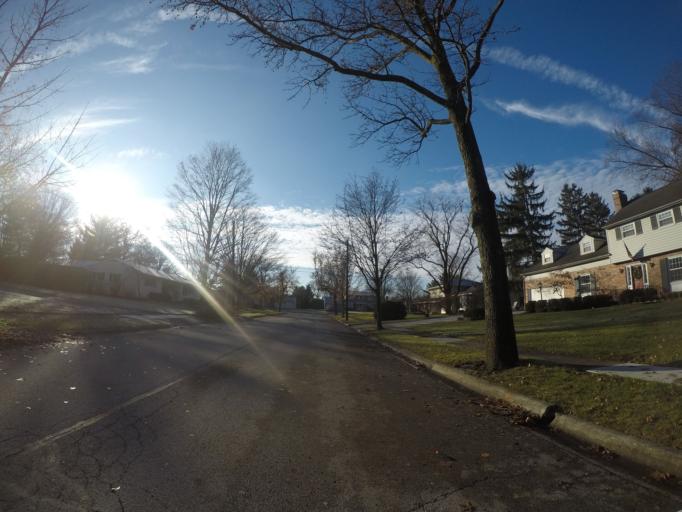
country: US
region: Ohio
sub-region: Franklin County
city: Upper Arlington
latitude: 40.0427
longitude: -83.0788
